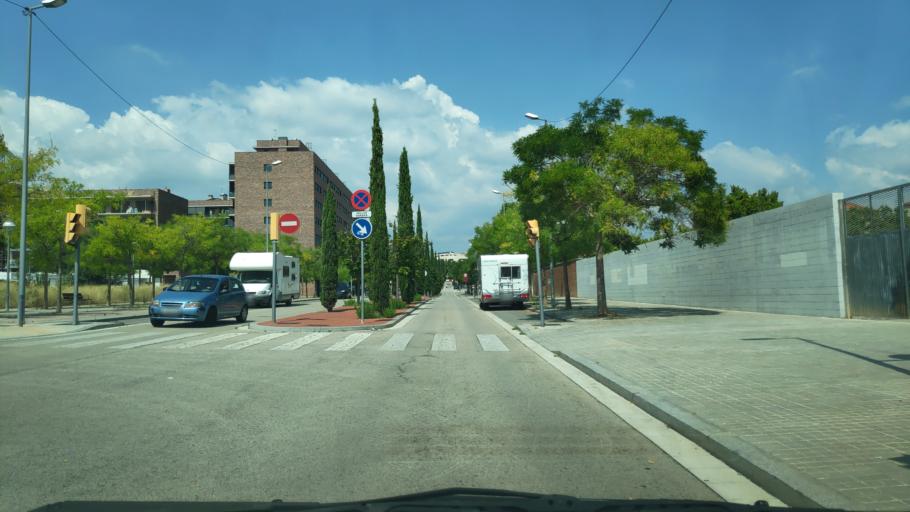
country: ES
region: Catalonia
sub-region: Provincia de Barcelona
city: Sant Quirze del Valles
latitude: 41.5462
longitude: 2.0848
